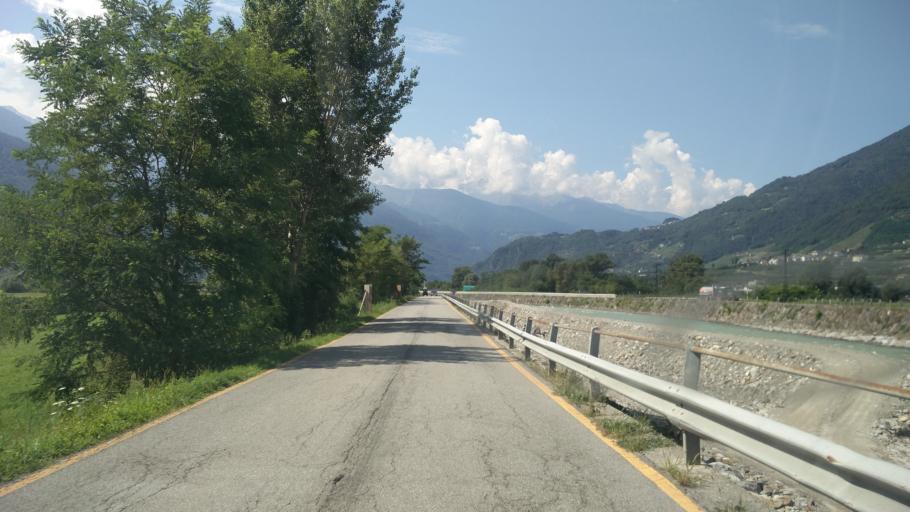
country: IT
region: Lombardy
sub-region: Provincia di Sondrio
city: Villa
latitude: 46.1951
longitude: 10.1376
